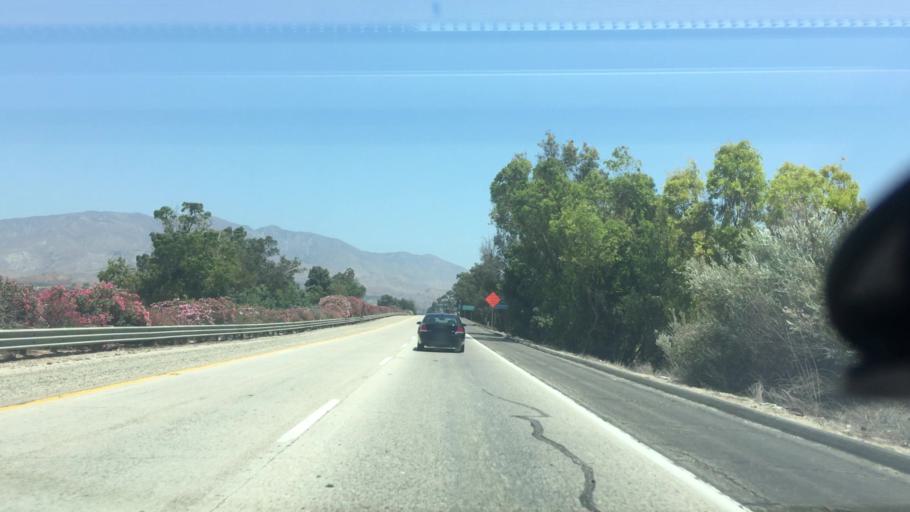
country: US
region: California
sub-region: Ventura County
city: Santa Paula
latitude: 34.3316
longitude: -119.0895
